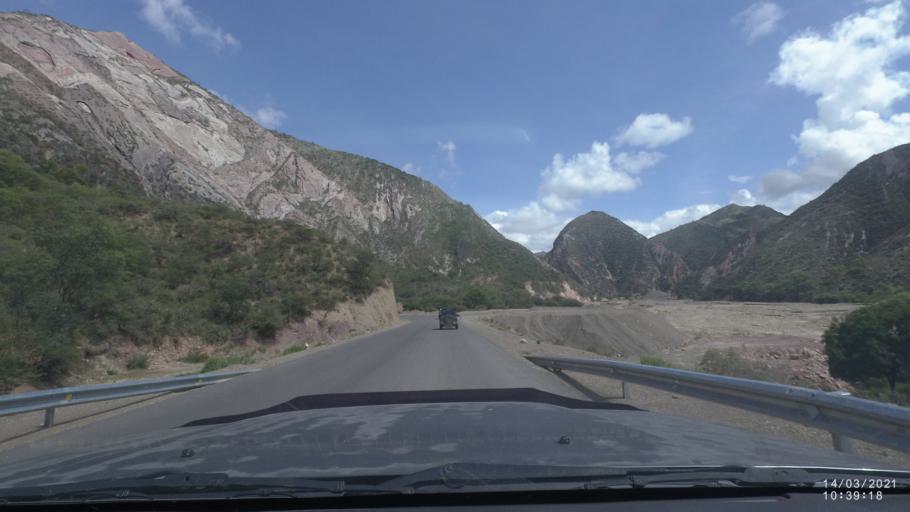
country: BO
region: Cochabamba
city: Cliza
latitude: -17.8884
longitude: -65.8969
